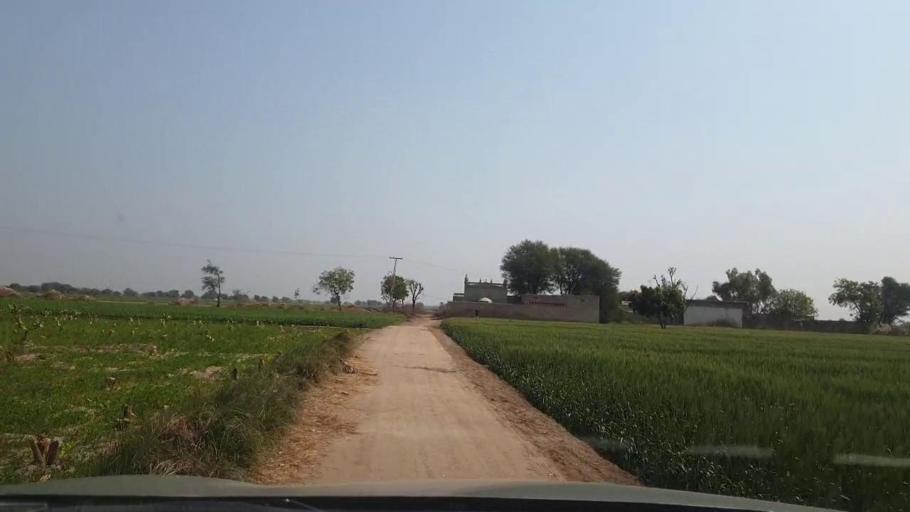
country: PK
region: Sindh
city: Tando Allahyar
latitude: 25.5338
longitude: 68.7931
